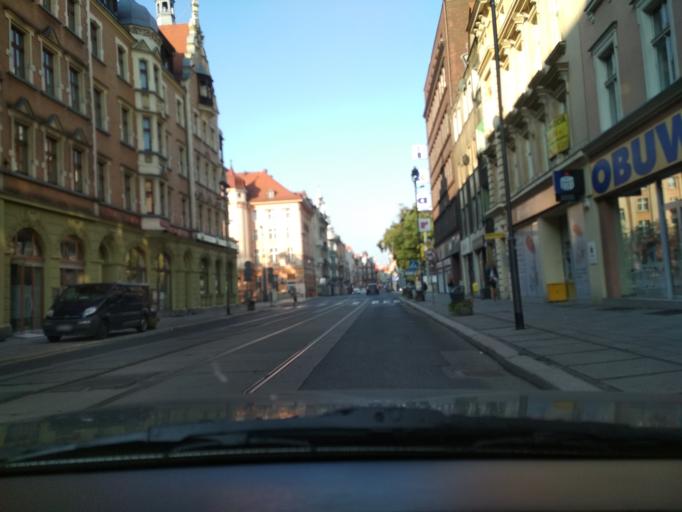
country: PL
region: Silesian Voivodeship
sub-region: Gliwice
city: Gliwice
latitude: 50.2969
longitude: 18.6711
